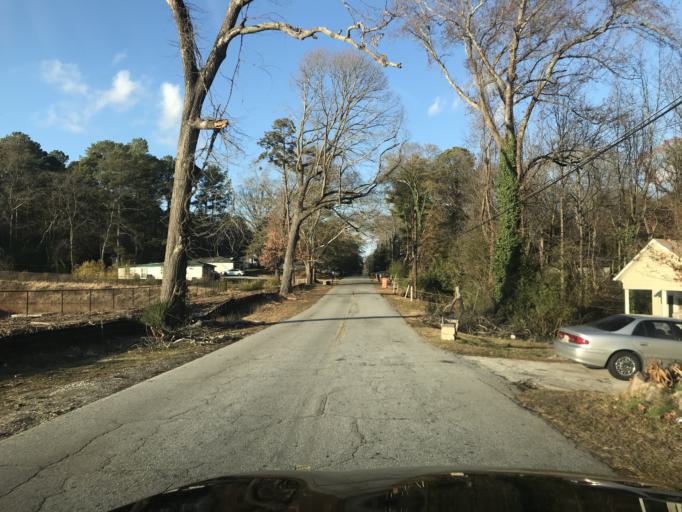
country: US
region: Georgia
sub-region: Fulton County
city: College Park
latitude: 33.6283
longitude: -84.4841
